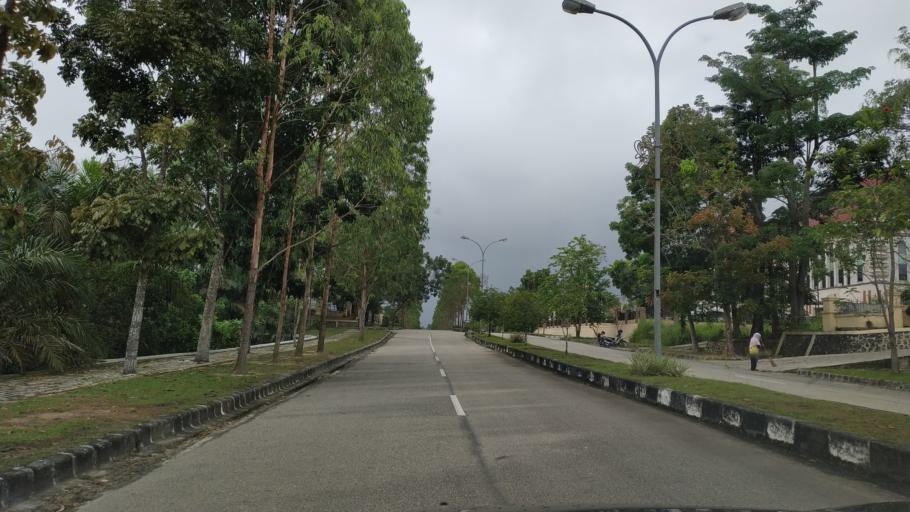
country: ID
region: Riau
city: Pangkalanbunut
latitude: 0.3829
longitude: 101.8279
